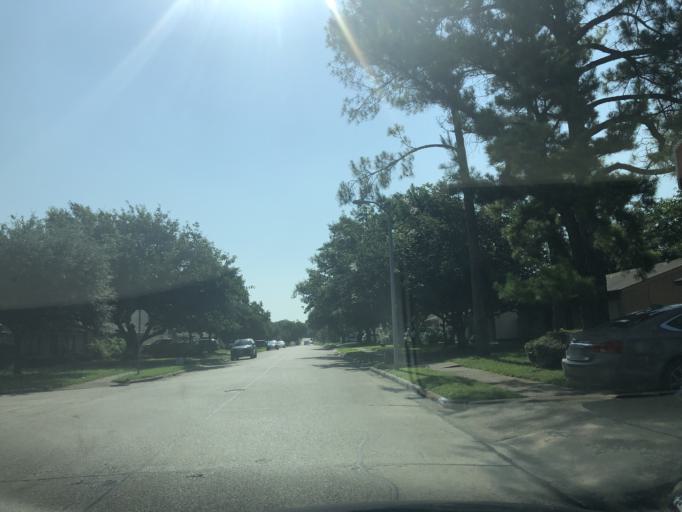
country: US
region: Texas
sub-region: Dallas County
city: Irving
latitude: 32.7969
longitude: -96.9673
